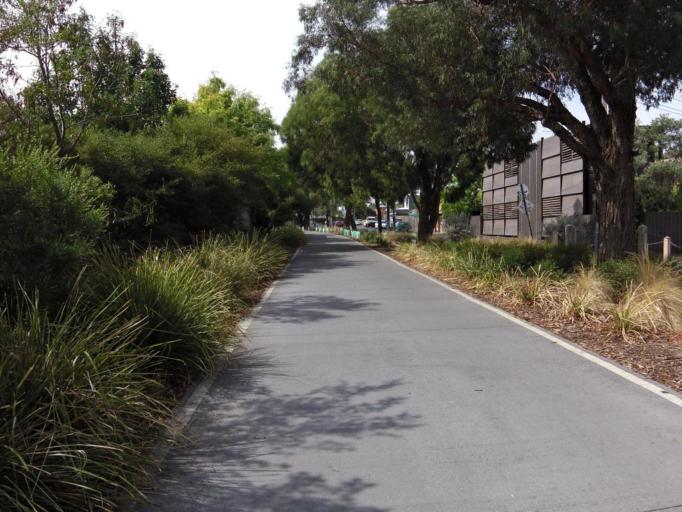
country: AU
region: Victoria
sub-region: Yarra
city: North Fitzroy
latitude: -37.7831
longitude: 144.9856
